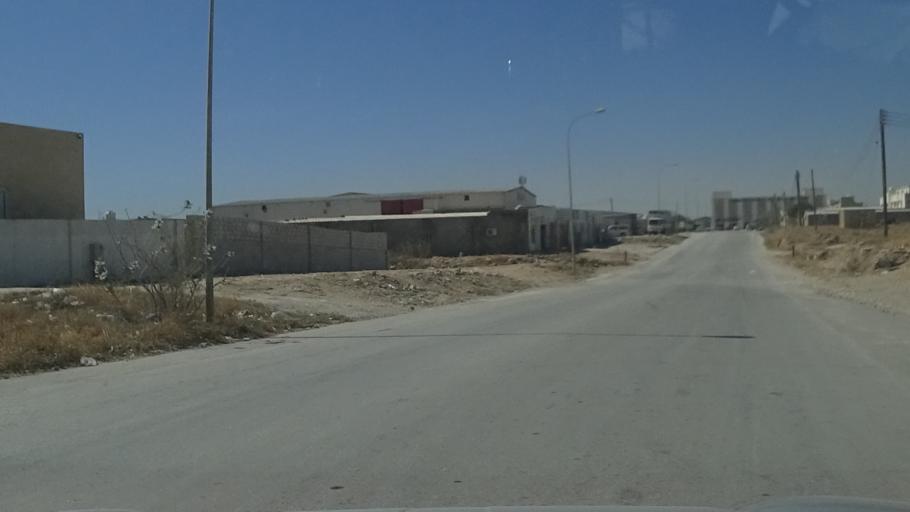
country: OM
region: Zufar
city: Salalah
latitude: 17.0332
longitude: 54.0416
